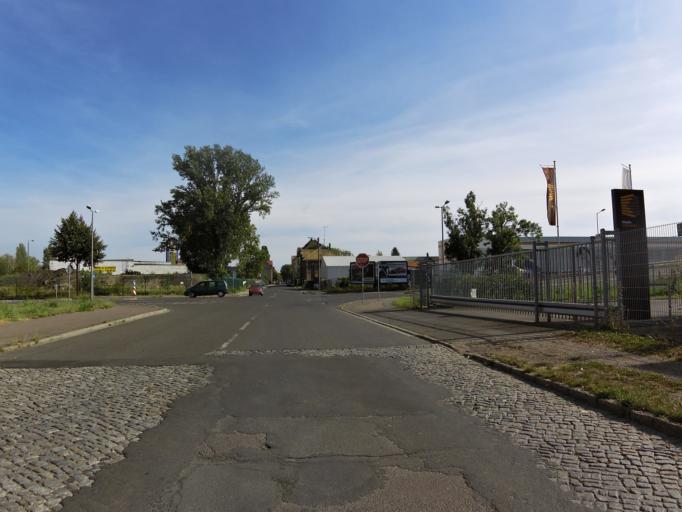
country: DE
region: Saxony
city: Leipzig
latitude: 51.3468
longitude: 12.3066
